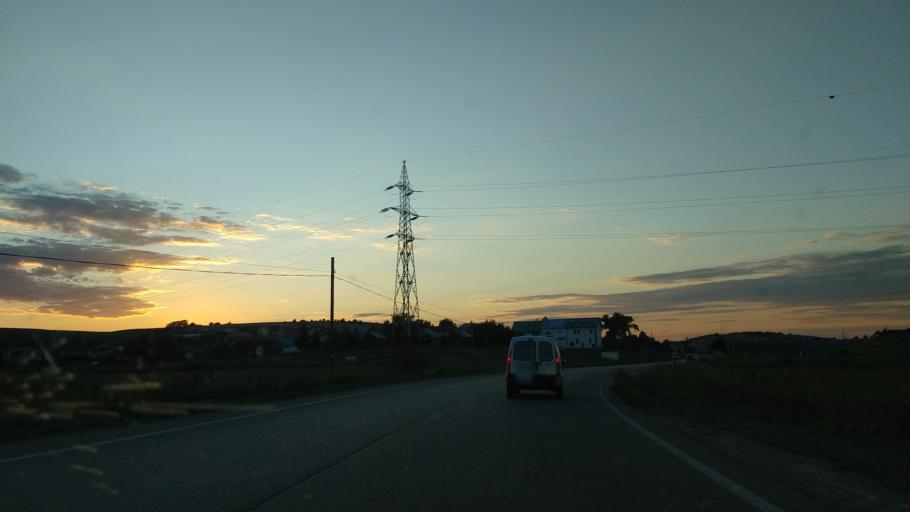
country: RO
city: Vanatori
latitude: 47.2286
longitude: 27.5378
